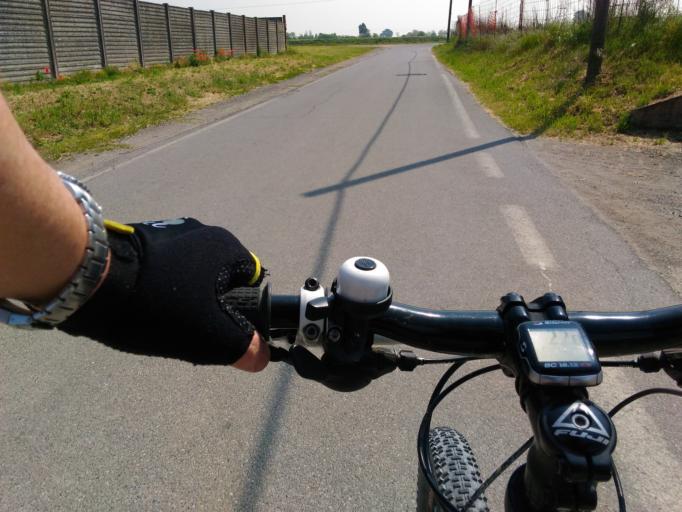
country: IT
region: Lombardy
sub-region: Provincia di Lodi
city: Castiraga Vidardo
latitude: 45.2590
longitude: 9.4189
